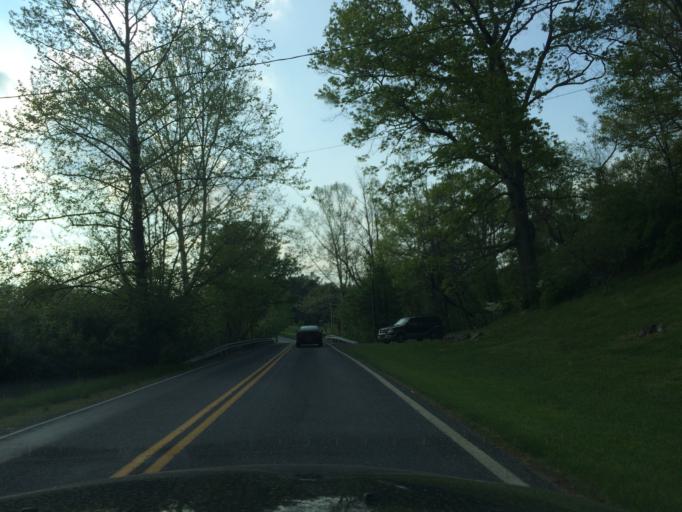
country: US
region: Maryland
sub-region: Carroll County
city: Sykesville
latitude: 39.2918
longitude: -77.0587
